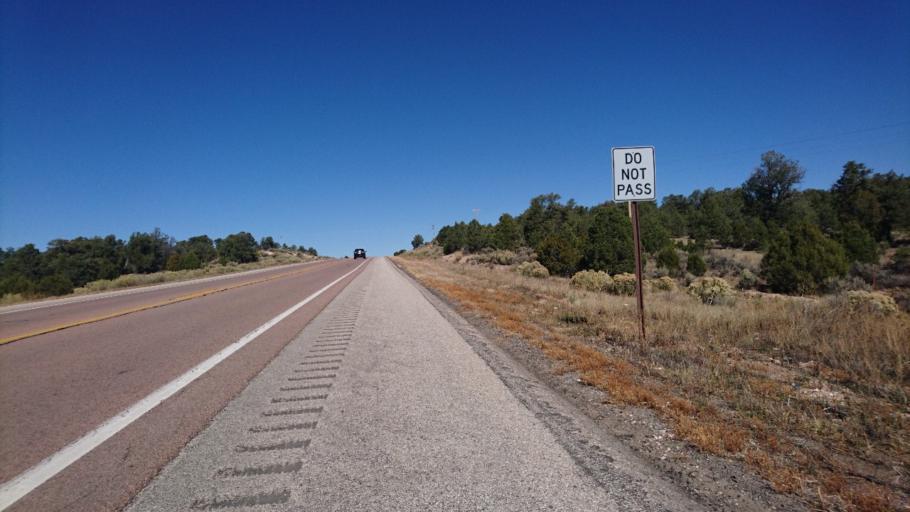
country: US
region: New Mexico
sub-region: McKinley County
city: Black Rock
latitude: 35.3059
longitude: -108.7576
